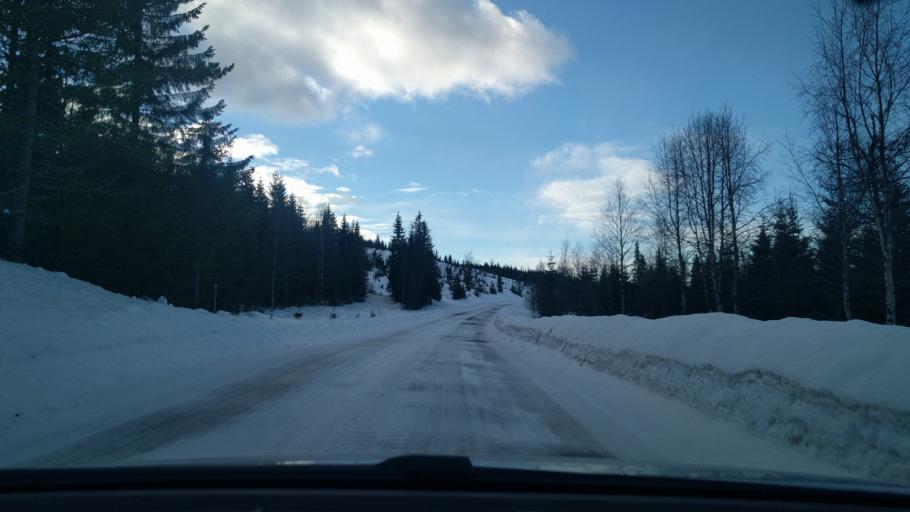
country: NO
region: Hedmark
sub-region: Trysil
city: Innbygda
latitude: 61.1089
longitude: 12.0939
